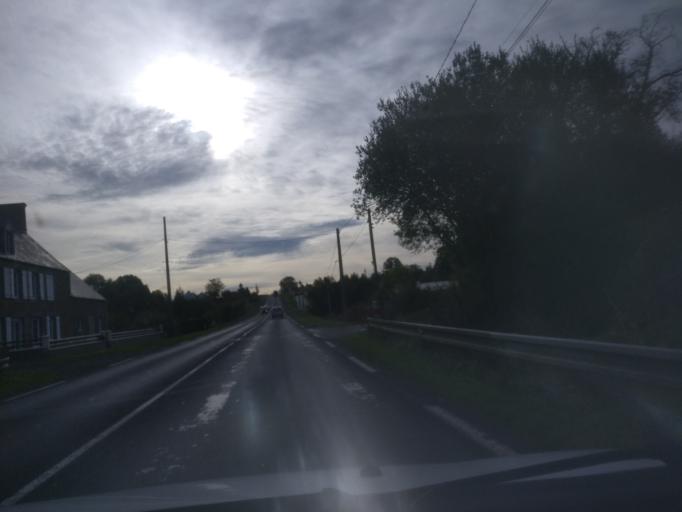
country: FR
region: Lower Normandy
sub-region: Departement de la Manche
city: Marcey-les-Greves
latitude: 48.7108
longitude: -1.3979
